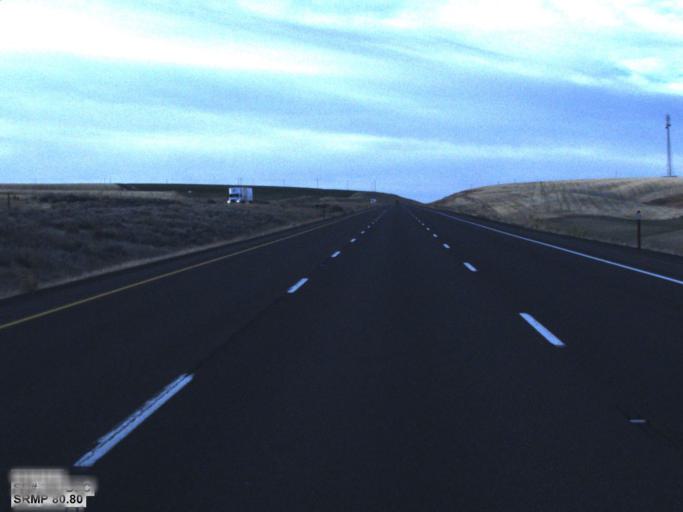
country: US
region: Washington
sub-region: Adams County
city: Ritzville
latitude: 46.9514
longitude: -118.5772
